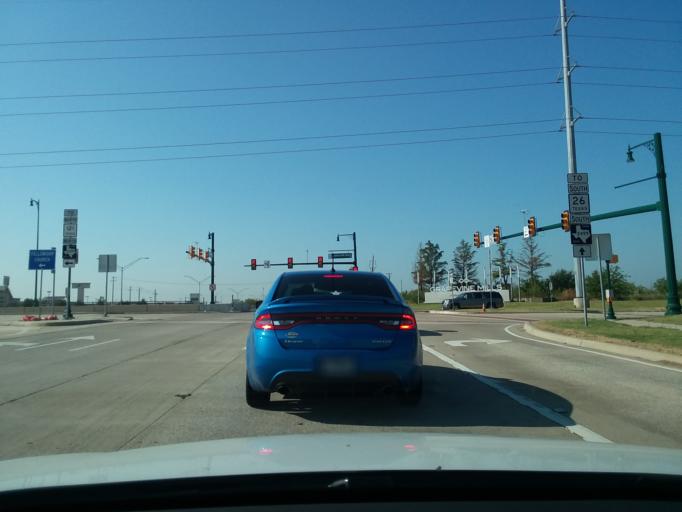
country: US
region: Texas
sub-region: Dallas County
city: Coppell
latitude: 32.9732
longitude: -97.0370
